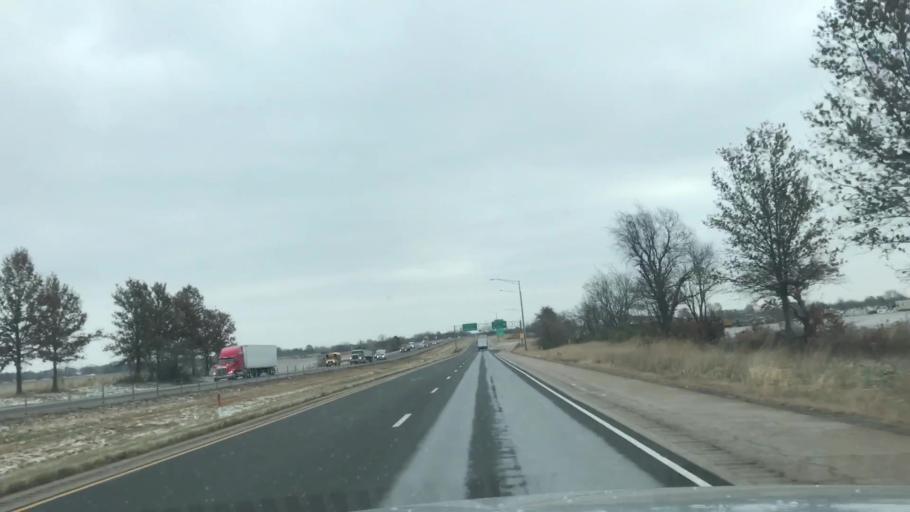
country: US
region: Illinois
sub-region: Madison County
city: Troy
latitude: 38.7518
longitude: -89.9164
